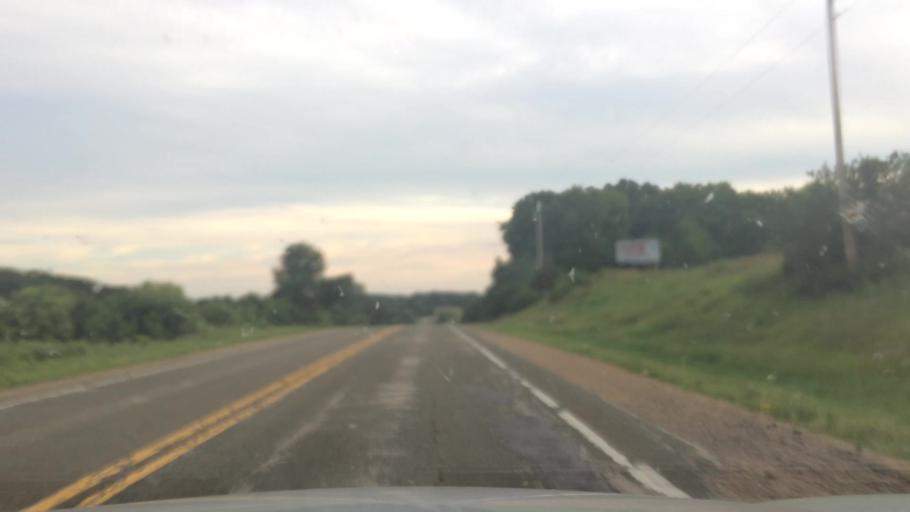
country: US
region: Wisconsin
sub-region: Columbia County
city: Lodi
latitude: 43.3289
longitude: -89.4850
